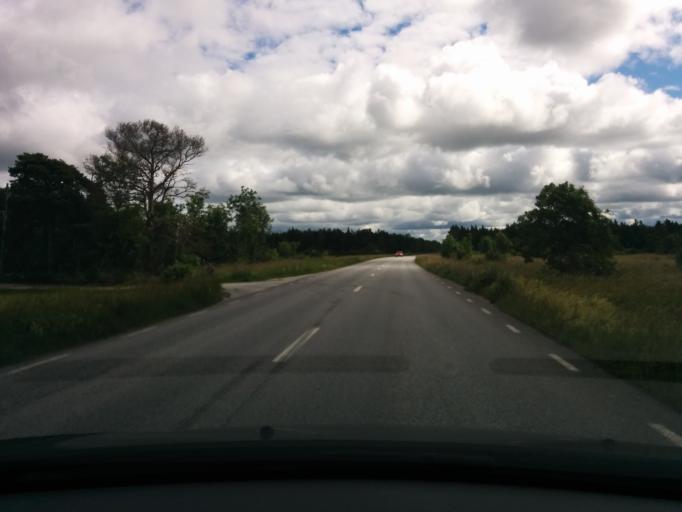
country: SE
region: Gotland
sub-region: Gotland
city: Visby
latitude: 57.6388
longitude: 18.4824
